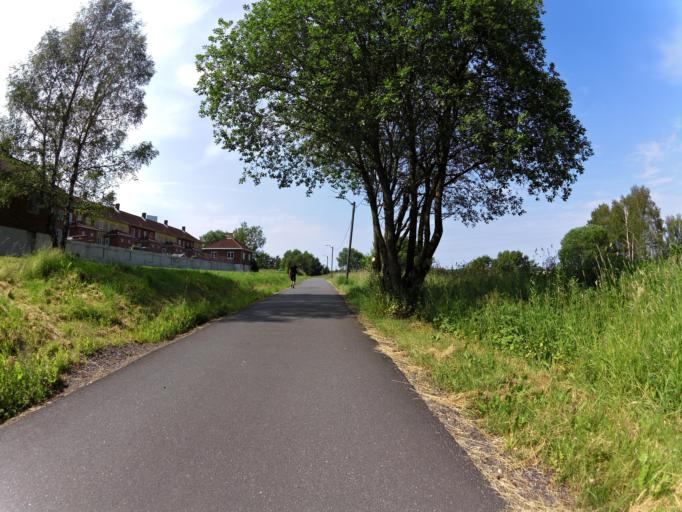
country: NO
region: Ostfold
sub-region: Sarpsborg
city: Sarpsborg
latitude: 59.2784
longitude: 11.1312
